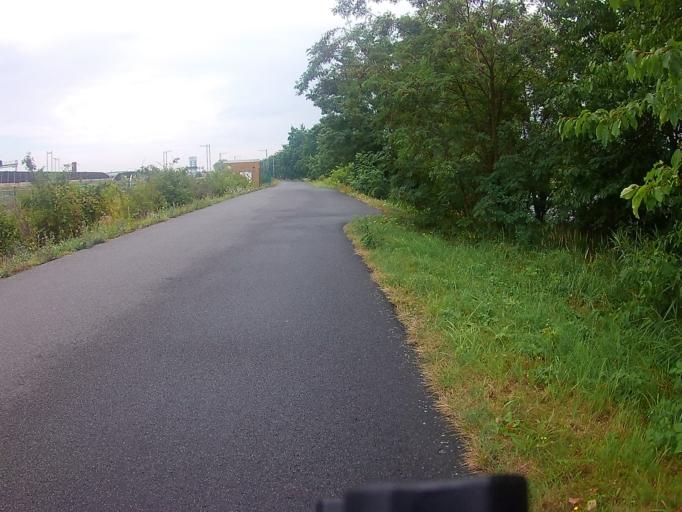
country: DE
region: Berlin
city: Johannisthal
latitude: 52.4277
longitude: 13.5119
